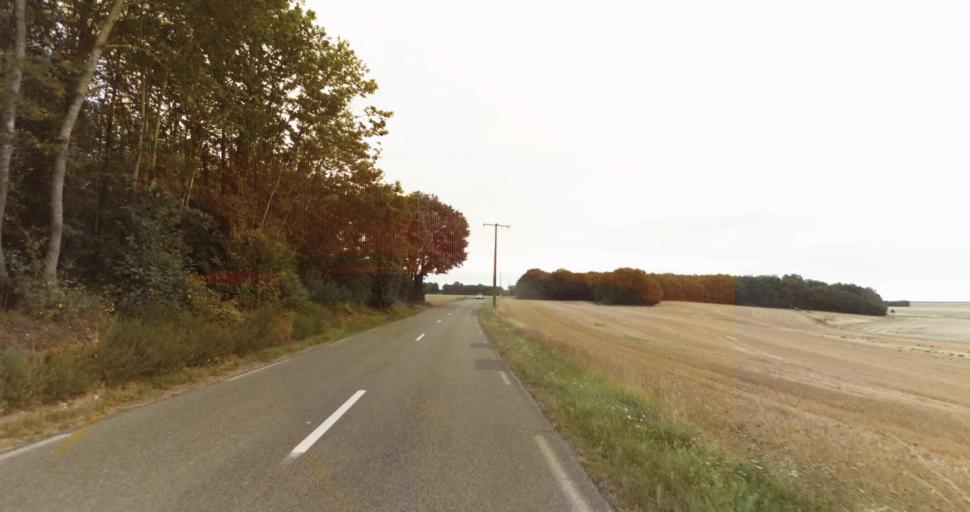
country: FR
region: Haute-Normandie
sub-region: Departement de l'Eure
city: Menilles
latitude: 48.9801
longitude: 1.2742
